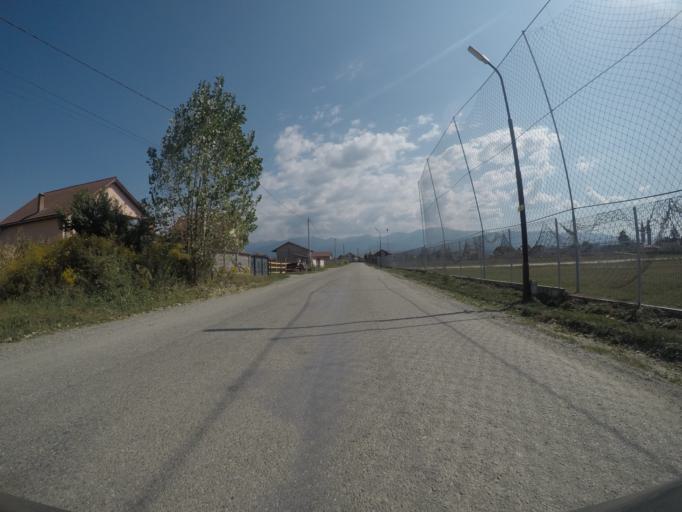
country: RO
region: Sibiu
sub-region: Comuna Avrig
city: Avrig
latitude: 45.7309
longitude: 24.3849
